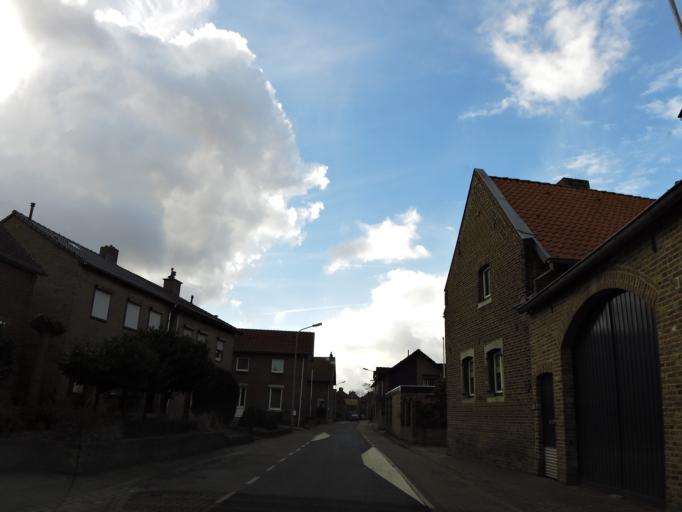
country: NL
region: Limburg
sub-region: Gemeente Maastricht
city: Maastricht
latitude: 50.8983
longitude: 5.6981
